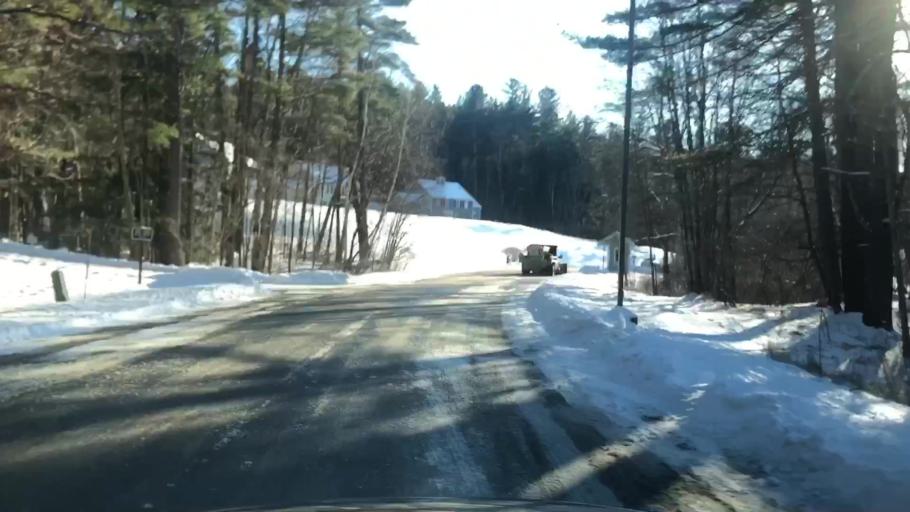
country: US
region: New Hampshire
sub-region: Hillsborough County
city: Milford
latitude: 42.8148
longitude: -71.6869
